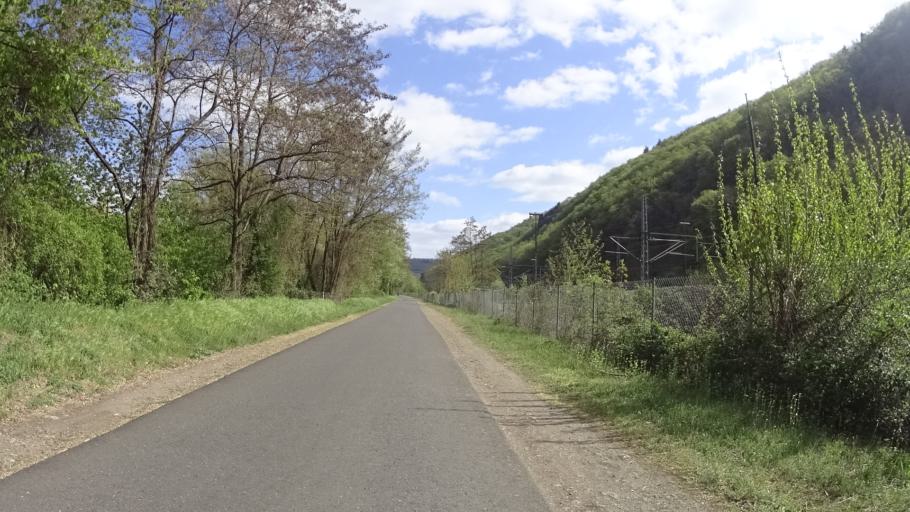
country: DE
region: Rheinland-Pfalz
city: Weiler
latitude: 49.9735
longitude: 7.8697
